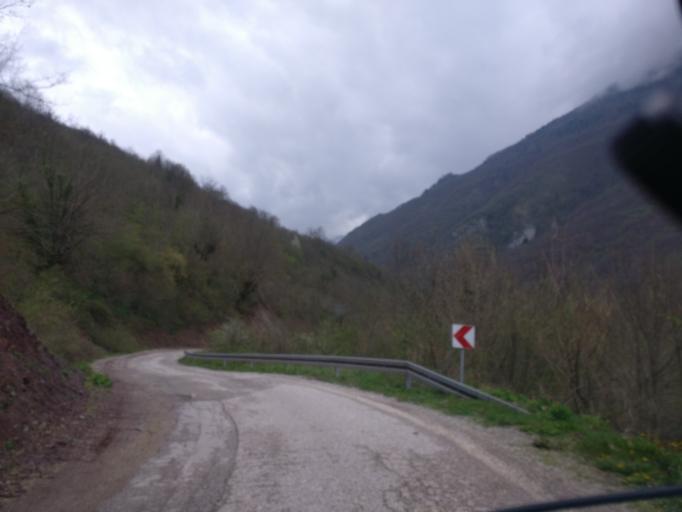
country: BA
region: Republika Srpska
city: Foca
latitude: 43.3584
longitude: 18.8148
